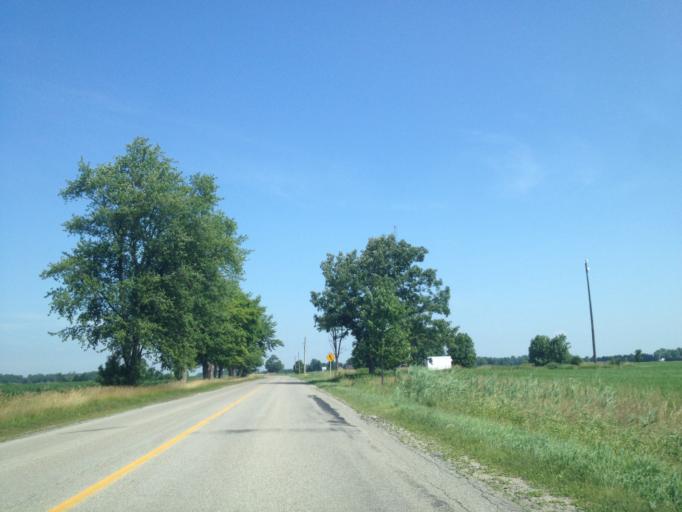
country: CA
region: Ontario
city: London
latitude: 43.0900
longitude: -81.2181
